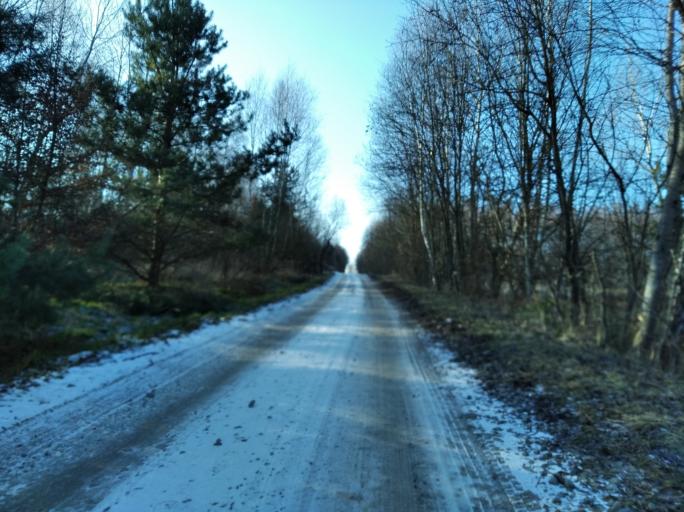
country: PL
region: Subcarpathian Voivodeship
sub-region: Powiat strzyzowski
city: Jawornik
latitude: 49.8308
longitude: 21.8638
